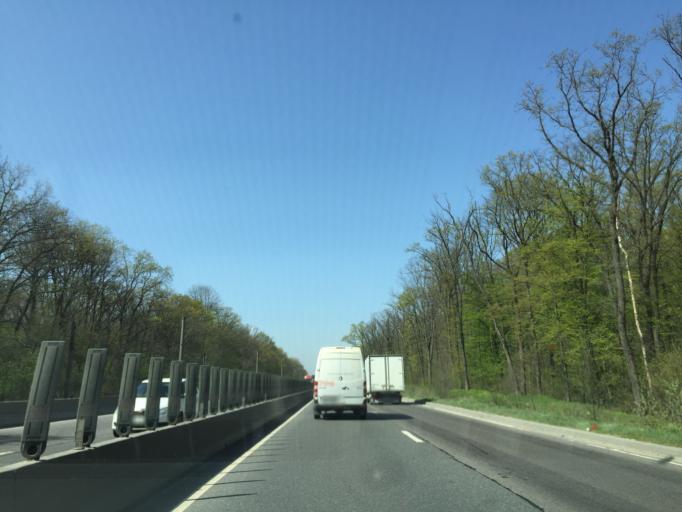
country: RO
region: Ilfov
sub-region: Comuna Tunari
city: Tunari
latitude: 44.5393
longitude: 26.1146
